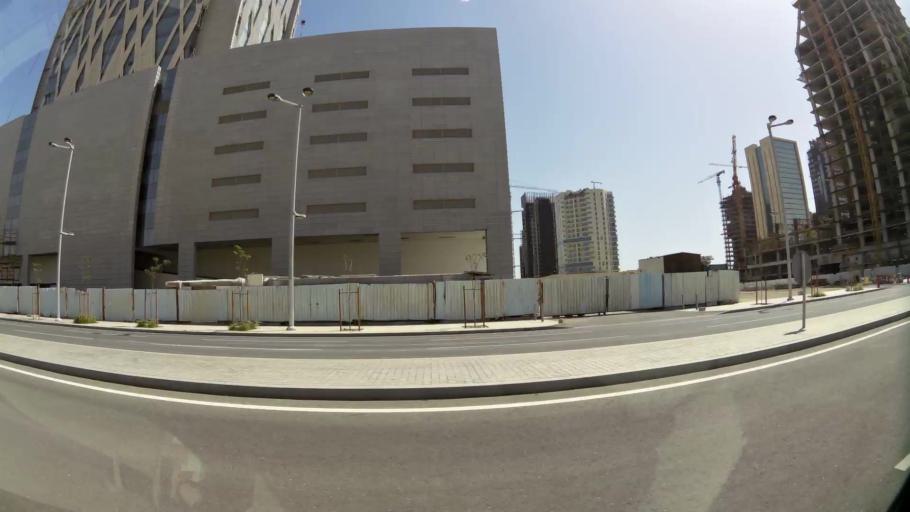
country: QA
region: Baladiyat ad Dawhah
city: Doha
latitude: 25.3909
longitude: 51.5195
